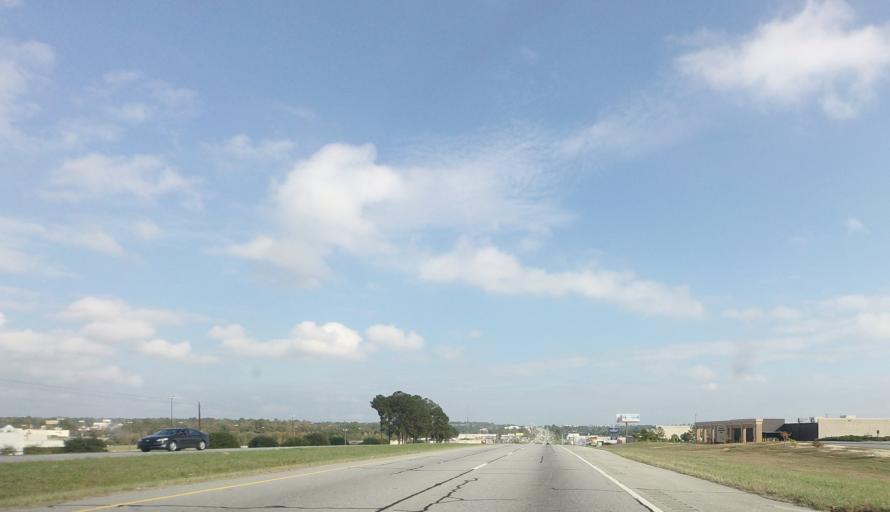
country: US
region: Georgia
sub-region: Bibb County
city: Macon
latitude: 32.8157
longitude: -83.6949
